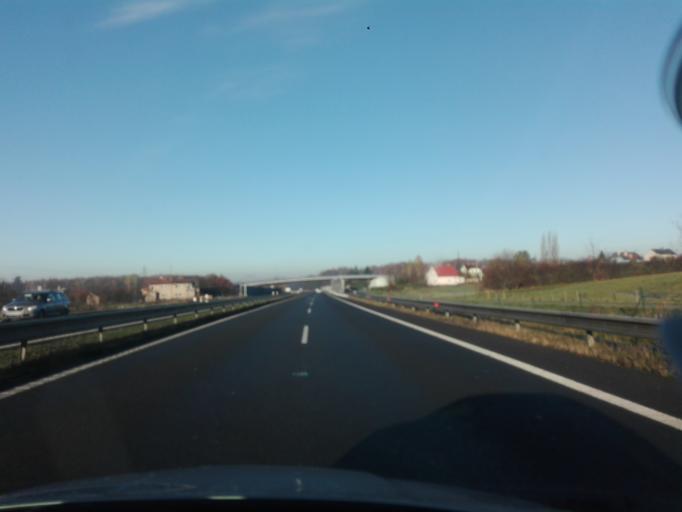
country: CZ
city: Dobra
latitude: 49.6775
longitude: 18.4106
